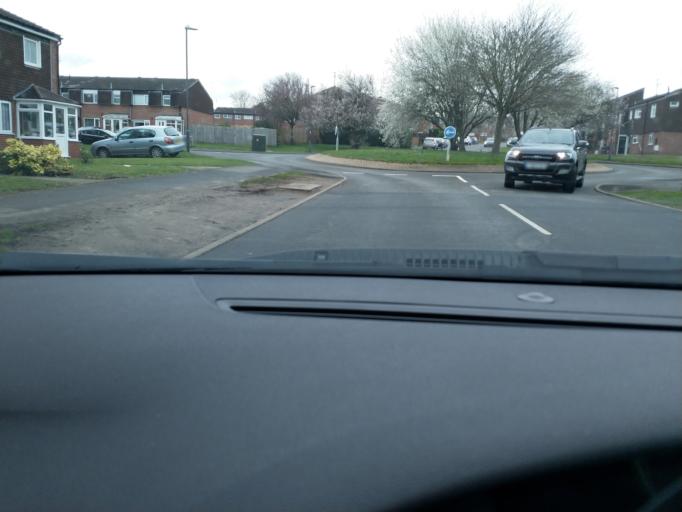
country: GB
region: England
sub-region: Warwickshire
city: Royal Leamington Spa
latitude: 52.2976
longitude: -1.5221
